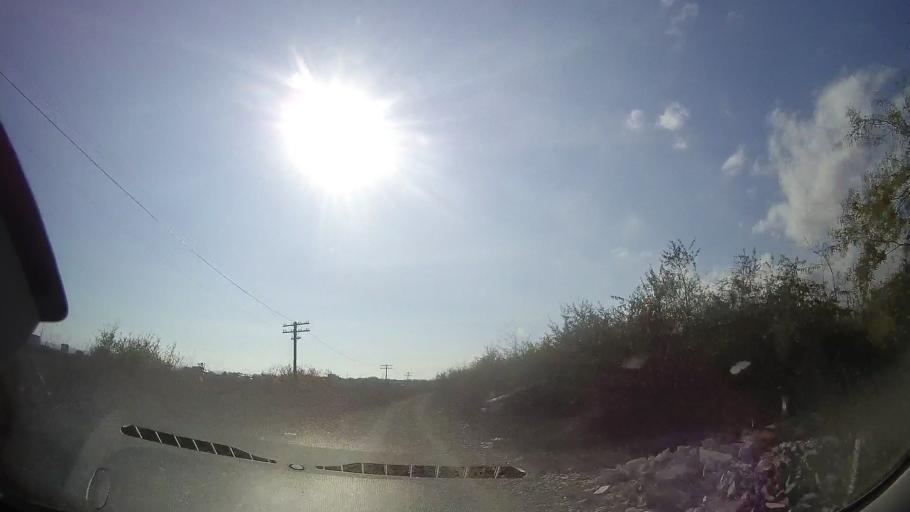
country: RO
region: Constanta
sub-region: Comuna Costinesti
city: Costinesti
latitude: 43.9696
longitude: 28.6423
